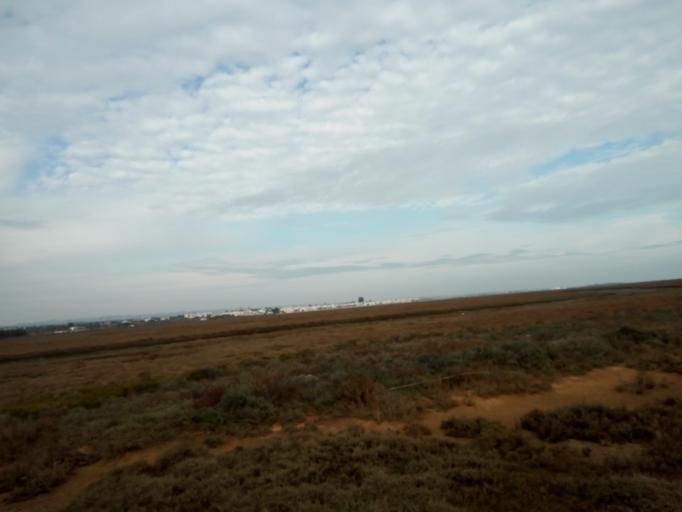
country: PT
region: Faro
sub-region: Tavira
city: Luz
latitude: 37.0894
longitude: -7.6703
